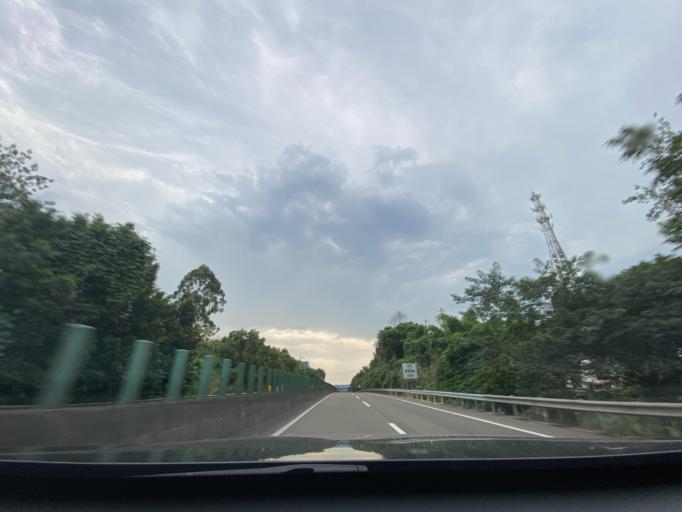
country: CN
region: Sichuan
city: Chonglong
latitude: 29.7276
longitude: 104.9203
